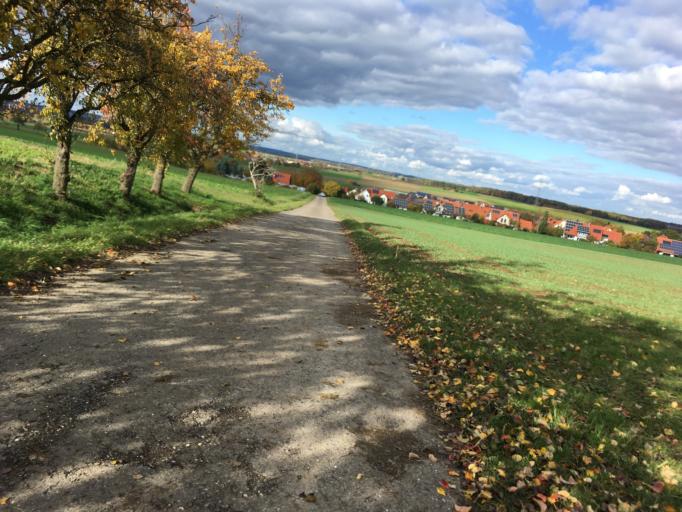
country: DE
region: Baden-Wuerttemberg
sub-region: Regierungsbezirk Stuttgart
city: Untermunkheim
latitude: 49.1986
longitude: 9.7394
